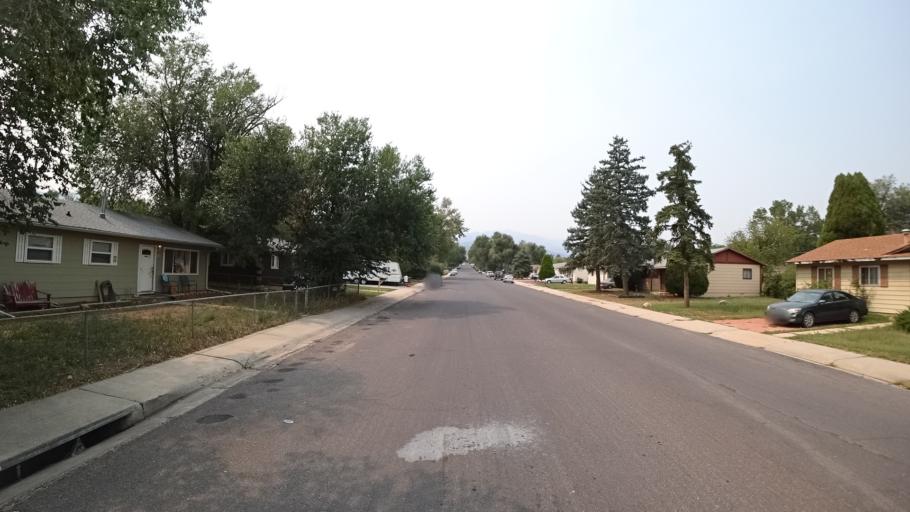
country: US
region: Colorado
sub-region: El Paso County
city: Colorado Springs
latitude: 38.8002
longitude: -104.8113
